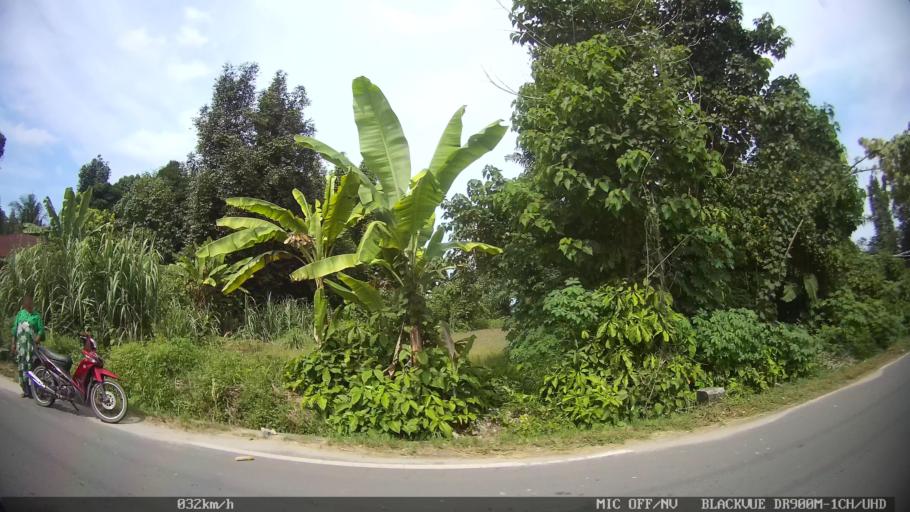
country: ID
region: North Sumatra
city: Percut
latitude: 3.6044
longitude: 98.8566
